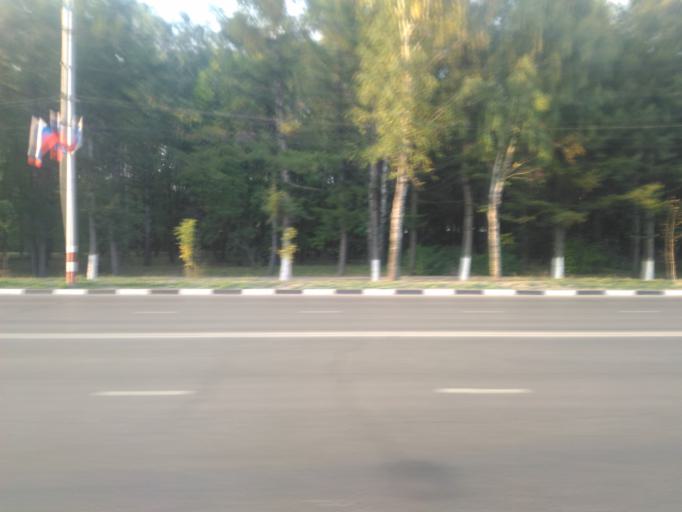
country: RU
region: Ulyanovsk
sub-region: Ulyanovskiy Rayon
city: Ulyanovsk
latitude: 54.3074
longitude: 48.3445
